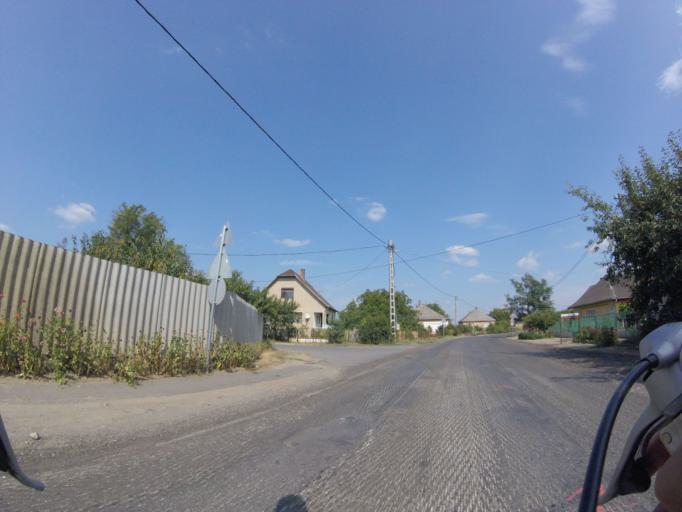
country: HU
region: Szabolcs-Szatmar-Bereg
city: Gyulahaza
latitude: 48.1534
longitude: 22.1443
